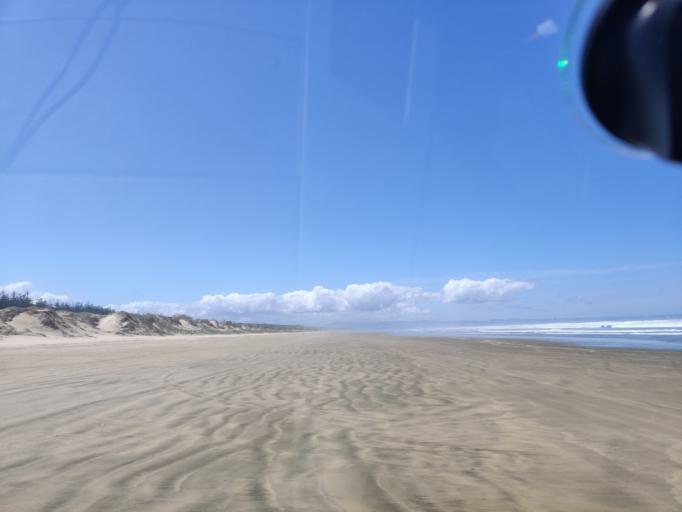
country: NZ
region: Northland
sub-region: Far North District
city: Kaitaia
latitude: -34.9807
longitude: 173.1410
